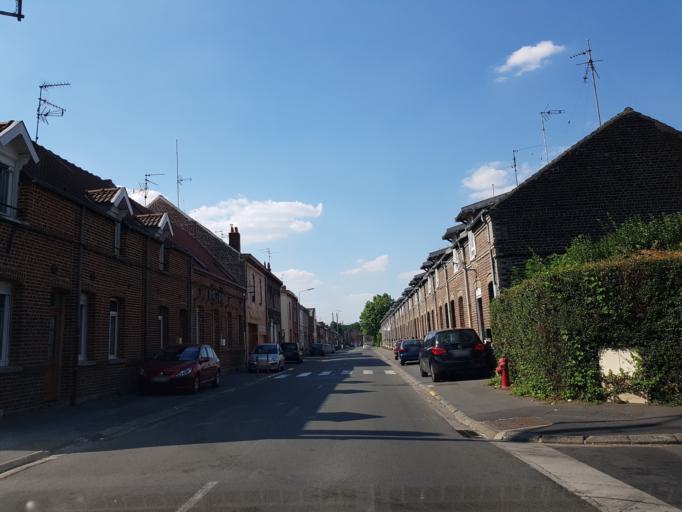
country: FR
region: Nord-Pas-de-Calais
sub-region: Departement du Nord
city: Lourches
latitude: 50.3138
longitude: 3.3440
